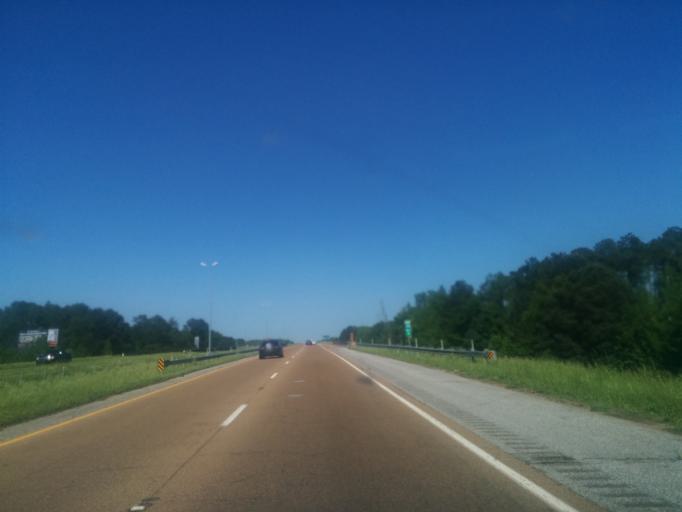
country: US
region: Mississippi
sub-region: Madison County
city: Ridgeland
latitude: 32.3825
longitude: -90.2023
